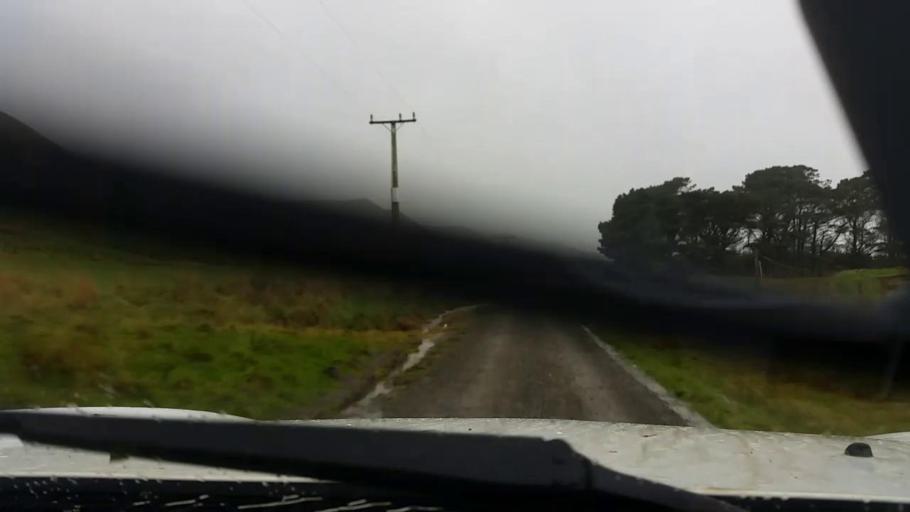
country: NZ
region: Wellington
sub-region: Masterton District
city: Masterton
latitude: -41.2539
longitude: 175.9109
